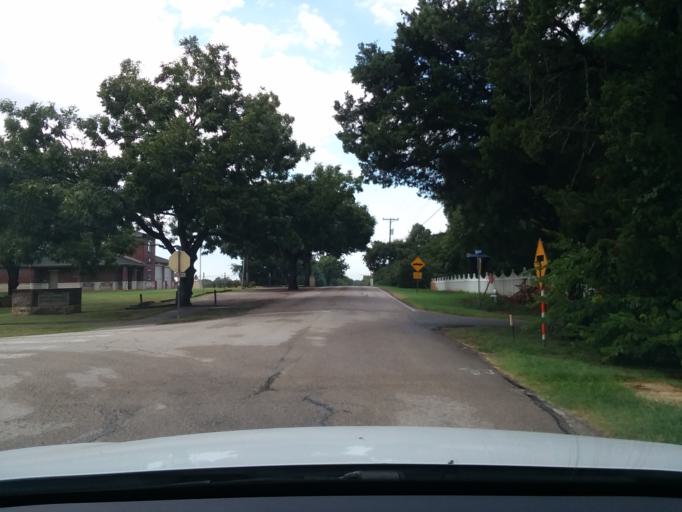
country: US
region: Texas
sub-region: Denton County
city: Double Oak
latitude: 33.0627
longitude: -97.0968
